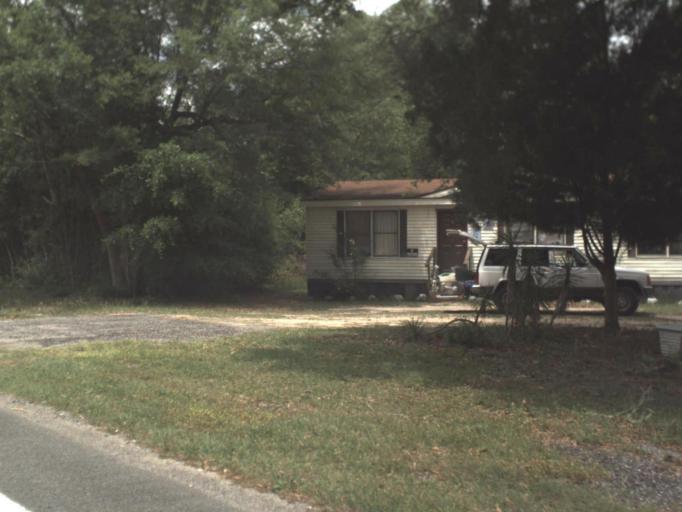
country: US
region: Florida
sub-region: Santa Rosa County
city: Point Baker
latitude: 30.6922
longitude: -87.0564
